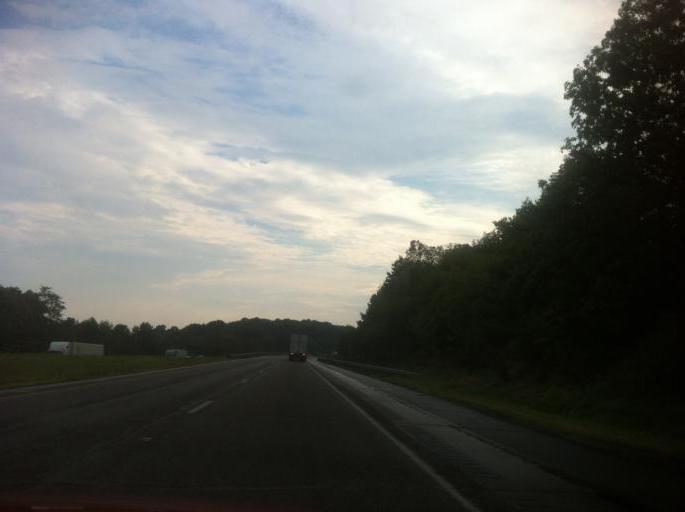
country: US
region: Pennsylvania
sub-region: Clarion County
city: Knox
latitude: 41.1897
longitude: -79.5945
